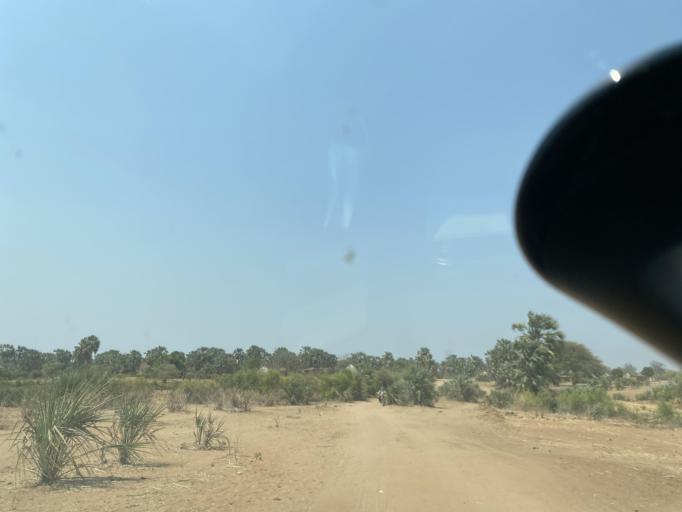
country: ZW
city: Chirundu
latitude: -16.1541
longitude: 28.8062
